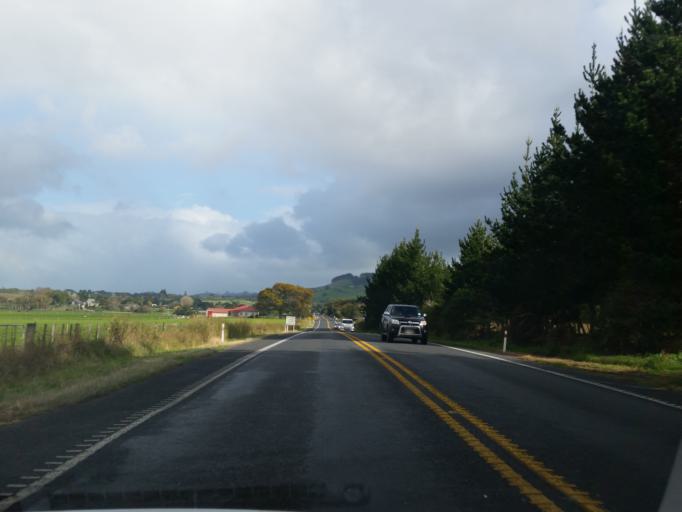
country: NZ
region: Auckland
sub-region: Auckland
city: Pukekohe East
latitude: -37.2148
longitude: 175.0661
